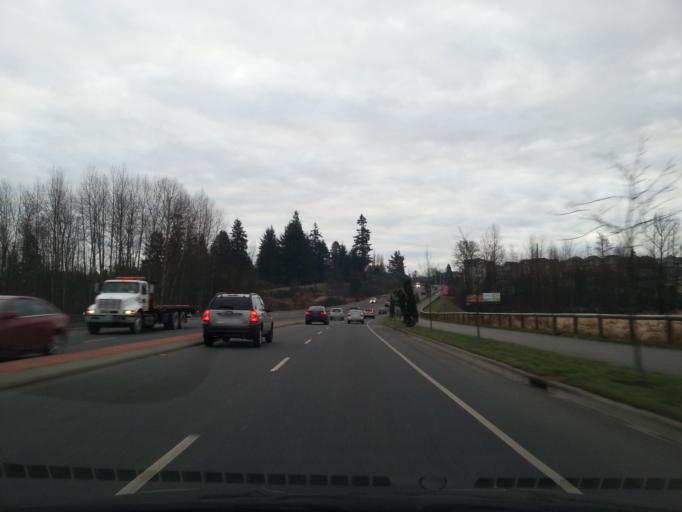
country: CA
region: British Columbia
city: Langley
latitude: 49.1354
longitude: -122.7286
